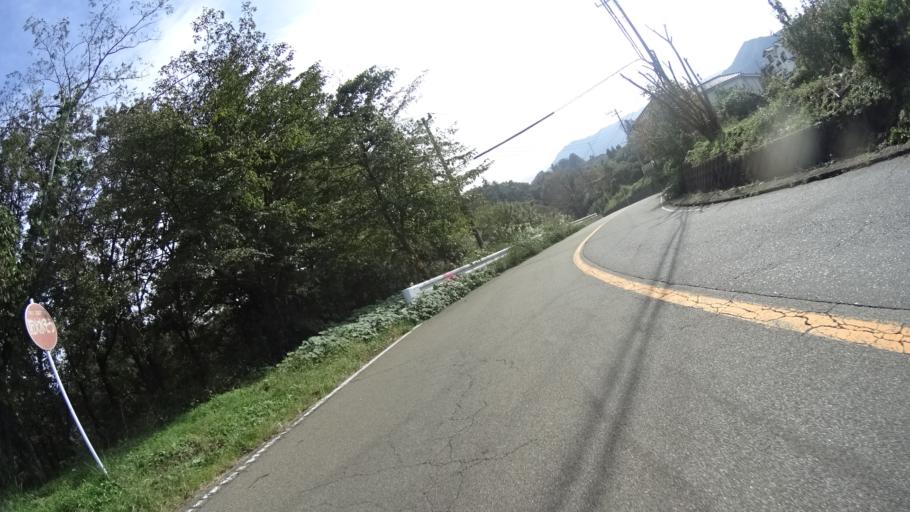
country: JP
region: Yamanashi
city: Uenohara
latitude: 35.5896
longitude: 139.1482
